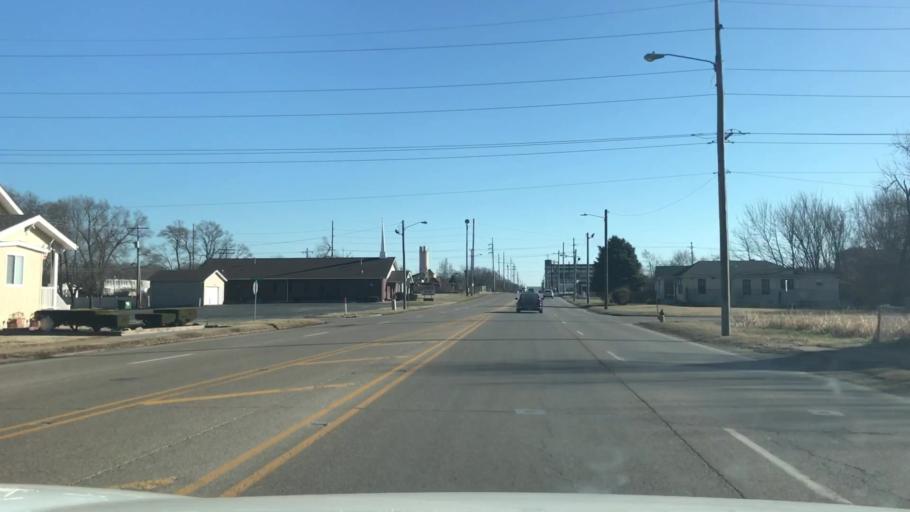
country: US
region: Illinois
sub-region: Saint Clair County
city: Alorton
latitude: 38.6048
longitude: -90.1338
